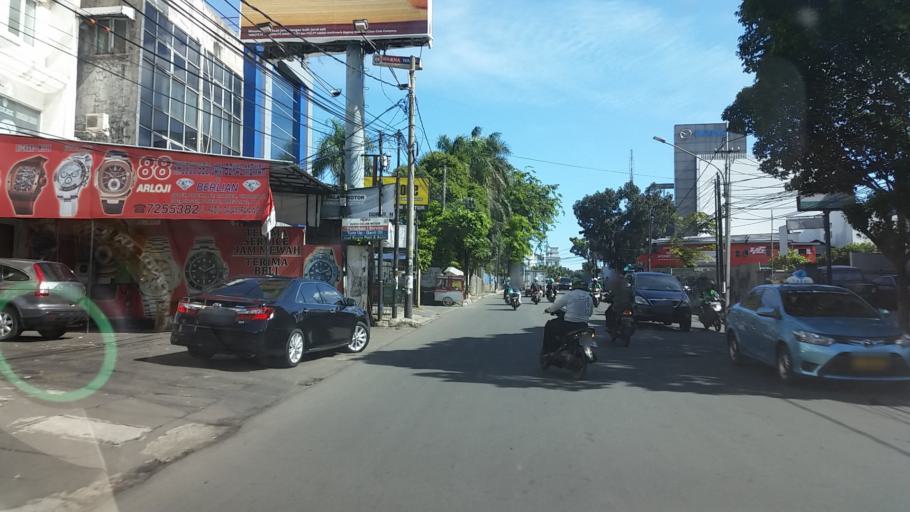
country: ID
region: Jakarta Raya
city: Jakarta
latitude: -6.2570
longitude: 106.7898
